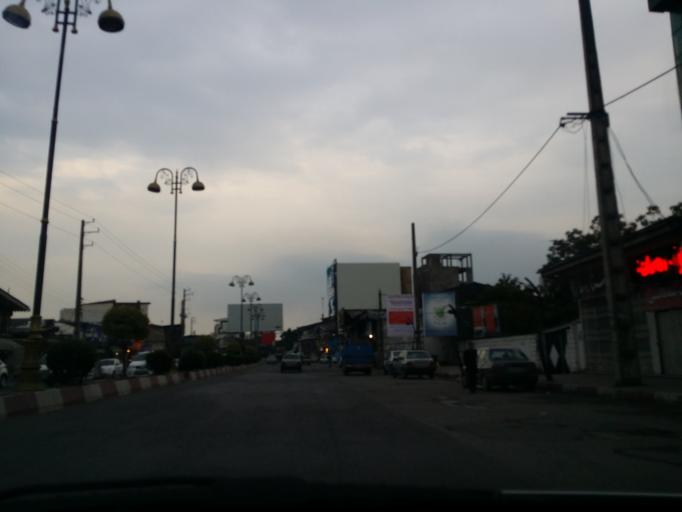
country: IR
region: Mazandaran
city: `Abbasabad
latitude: 36.7284
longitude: 51.1078
